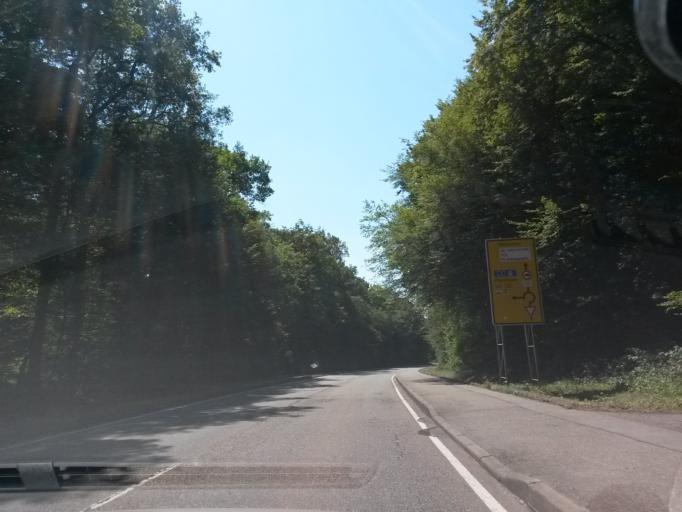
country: DE
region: Baden-Wuerttemberg
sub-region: Karlsruhe Region
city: Muhlacker
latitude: 48.9641
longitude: 8.8611
